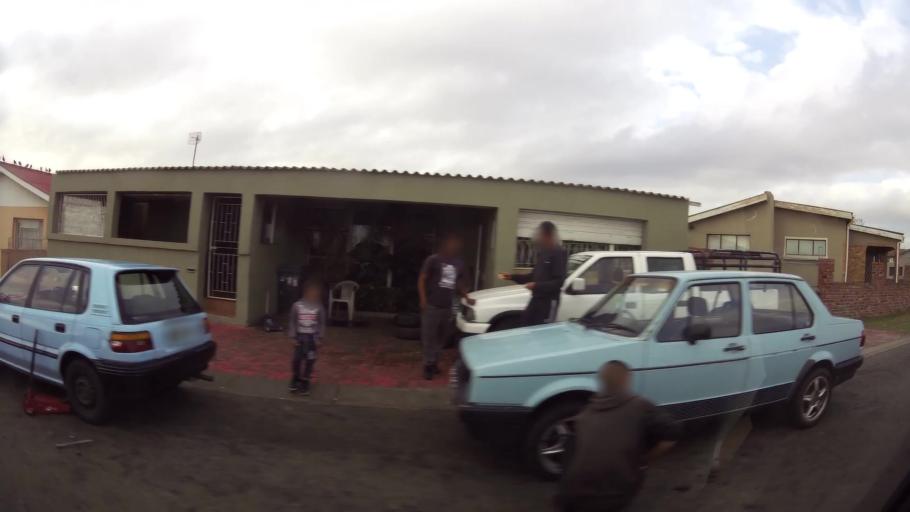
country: ZA
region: Eastern Cape
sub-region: Nelson Mandela Bay Metropolitan Municipality
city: Port Elizabeth
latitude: -33.9187
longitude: 25.5539
